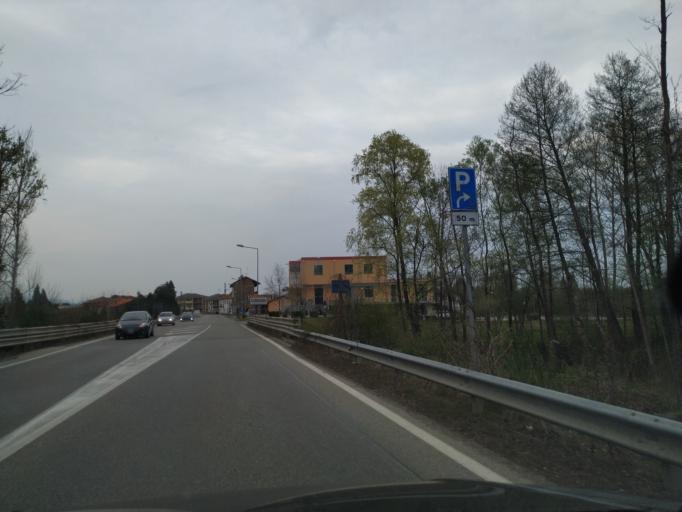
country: IT
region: Piedmont
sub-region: Provincia di Novara
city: Cureggio
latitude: 45.6703
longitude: 8.4540
